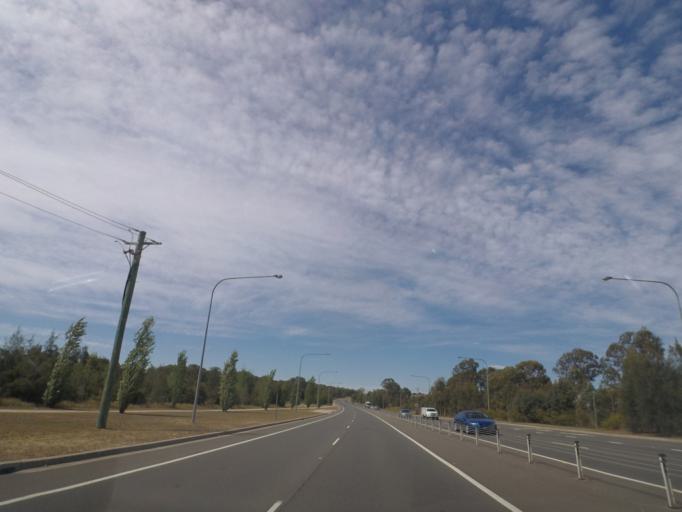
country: AU
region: New South Wales
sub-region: Camden
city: Narellan
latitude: -34.0360
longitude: 150.7466
